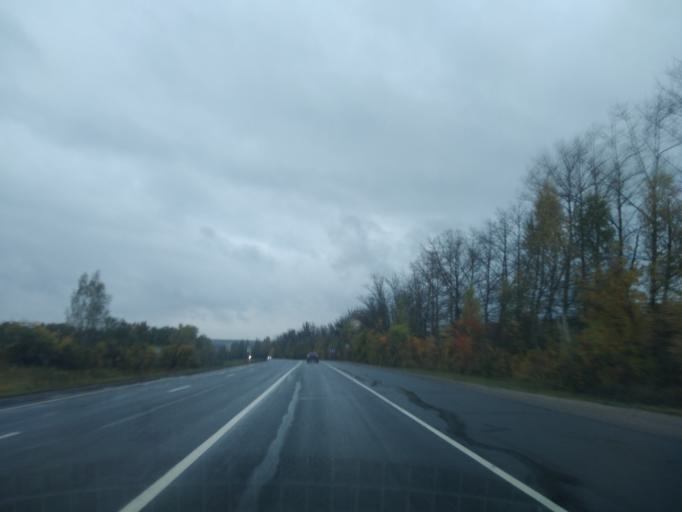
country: RU
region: Tula
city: Barsuki
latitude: 54.3096
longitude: 37.5399
